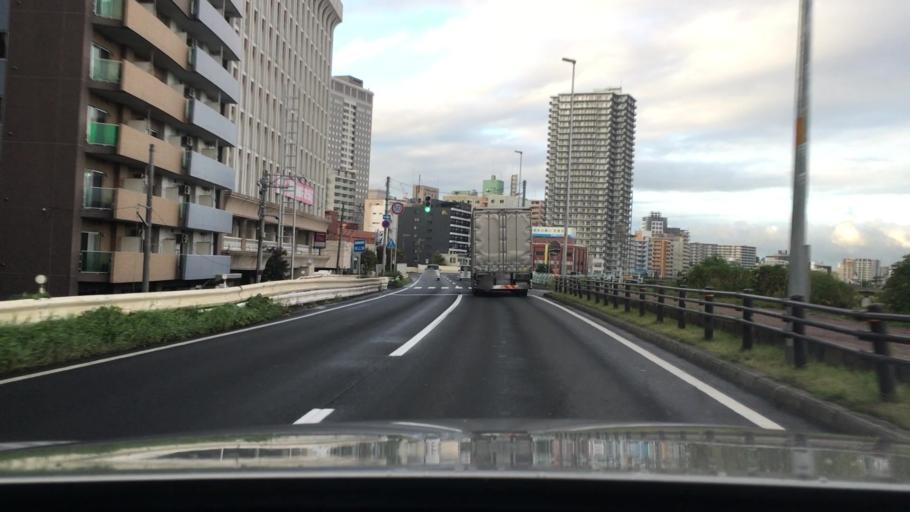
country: JP
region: Hokkaido
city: Sapporo
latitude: 43.0457
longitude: 141.3582
